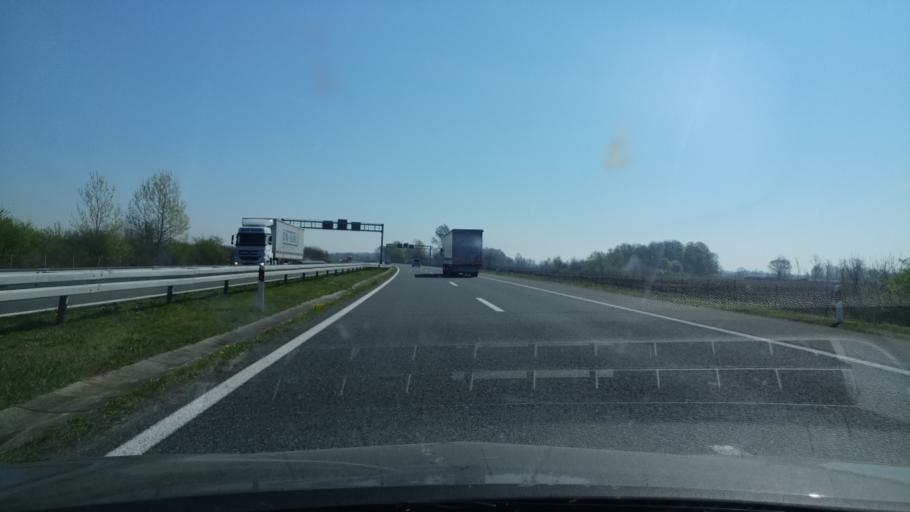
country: HR
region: Brodsko-Posavska
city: Garcin
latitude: 45.1549
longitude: 18.1965
